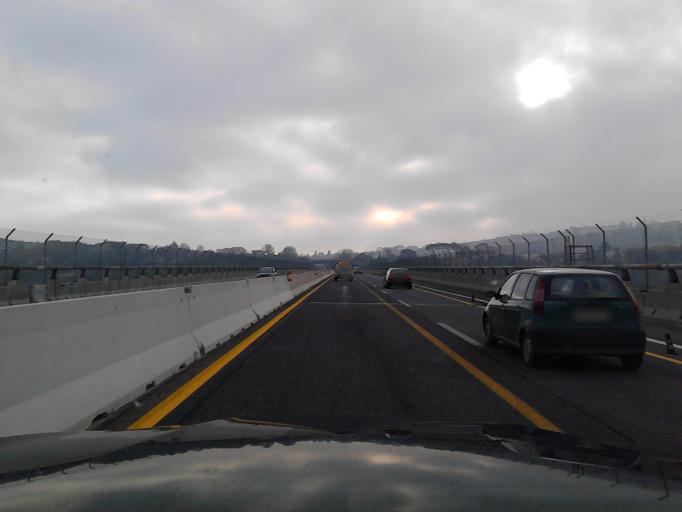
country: IT
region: Abruzzo
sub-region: Provincia di Teramo
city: Salino
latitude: 42.7756
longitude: 13.9317
